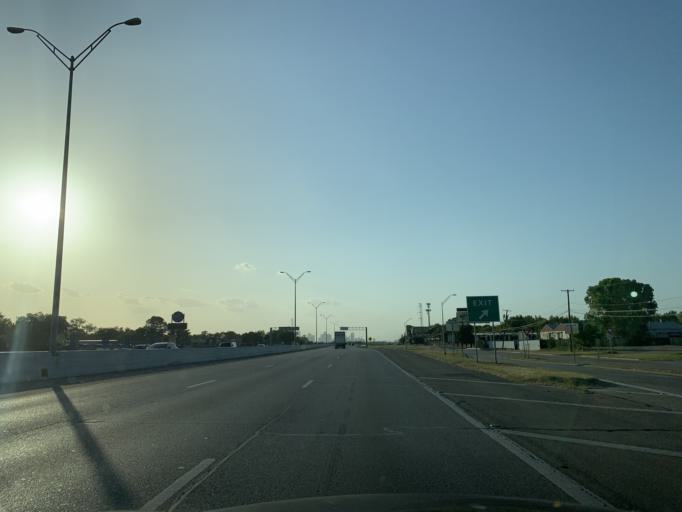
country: US
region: Texas
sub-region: Dallas County
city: Hutchins
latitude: 32.7283
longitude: -96.7056
